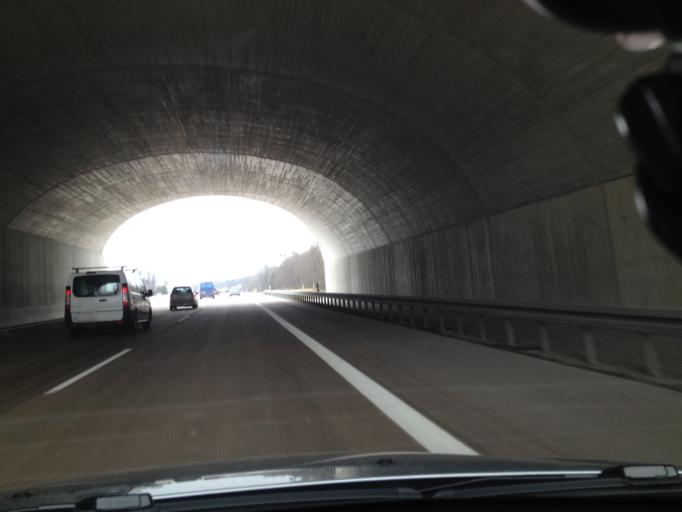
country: DE
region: Bavaria
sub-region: Swabia
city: Landensberg
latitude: 48.4054
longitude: 10.5223
